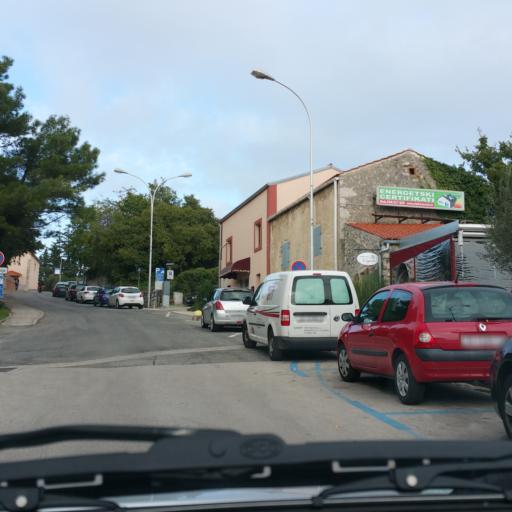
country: HR
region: Primorsko-Goranska
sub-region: Grad Krk
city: Krk
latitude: 45.0272
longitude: 14.5732
